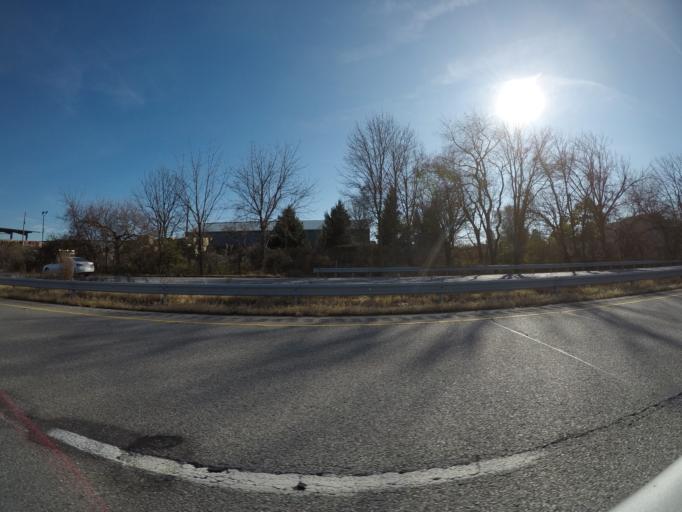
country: US
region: Pennsylvania
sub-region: Chester County
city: Parkesburg
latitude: 39.9868
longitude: -75.8852
